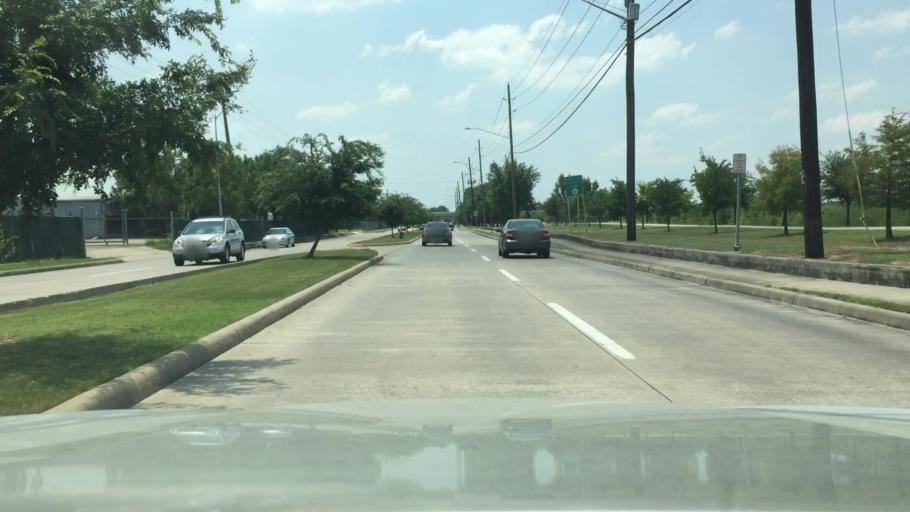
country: US
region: Texas
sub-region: Fort Bend County
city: Meadows Place
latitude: 29.7209
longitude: -95.5924
